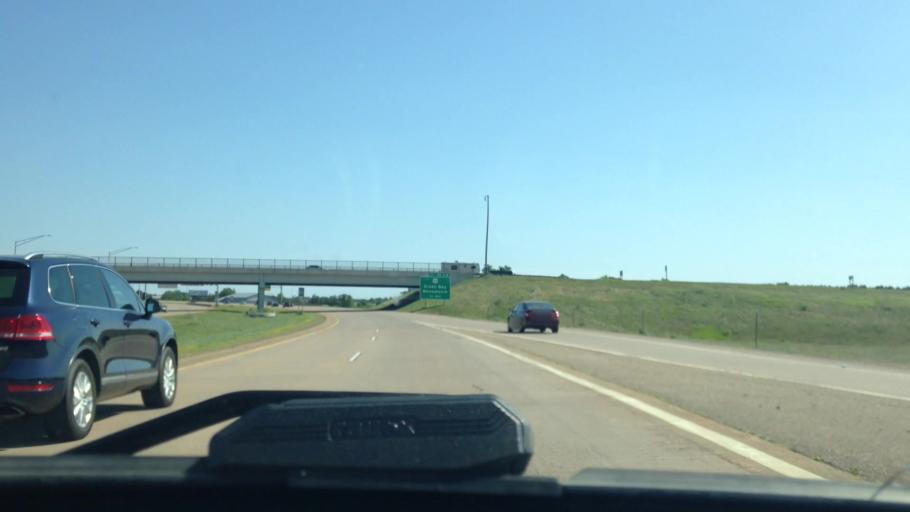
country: US
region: Wisconsin
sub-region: Chippewa County
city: Lake Hallie
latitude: 44.8805
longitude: -91.4148
